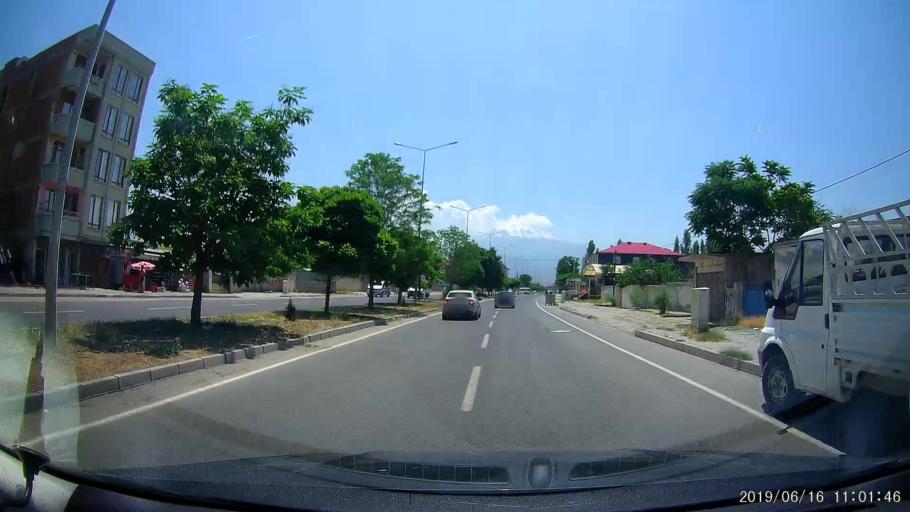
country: TR
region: Igdir
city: Igdir
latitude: 39.9127
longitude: 44.0533
